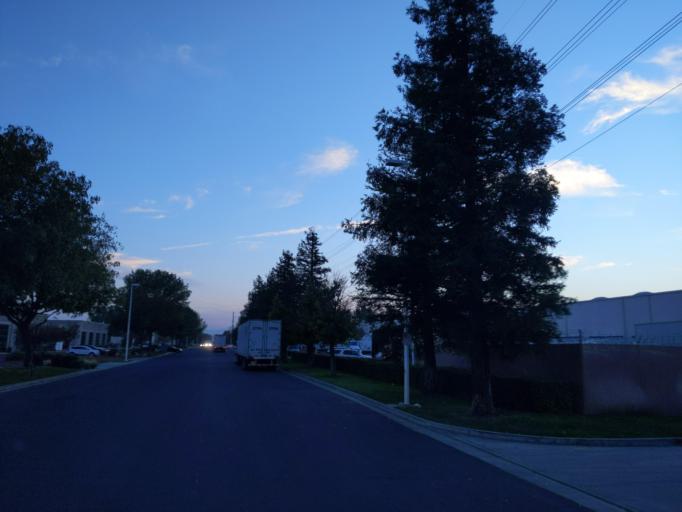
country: US
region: California
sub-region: San Joaquin County
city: Lathrop
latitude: 37.8044
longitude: -121.2921
